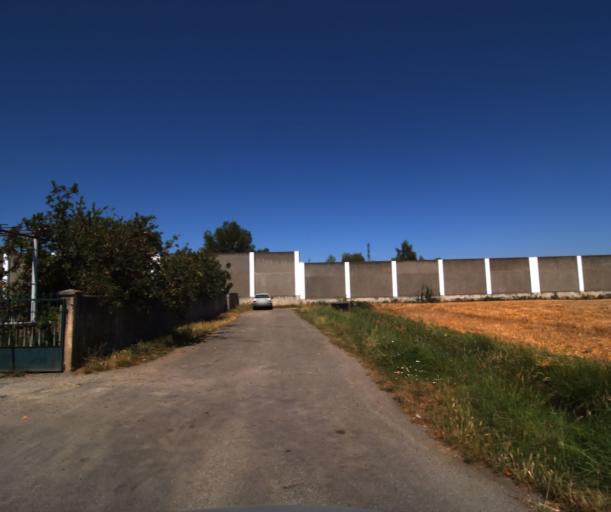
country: FR
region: Midi-Pyrenees
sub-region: Departement de la Haute-Garonne
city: Seysses
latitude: 43.4678
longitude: 1.3162
